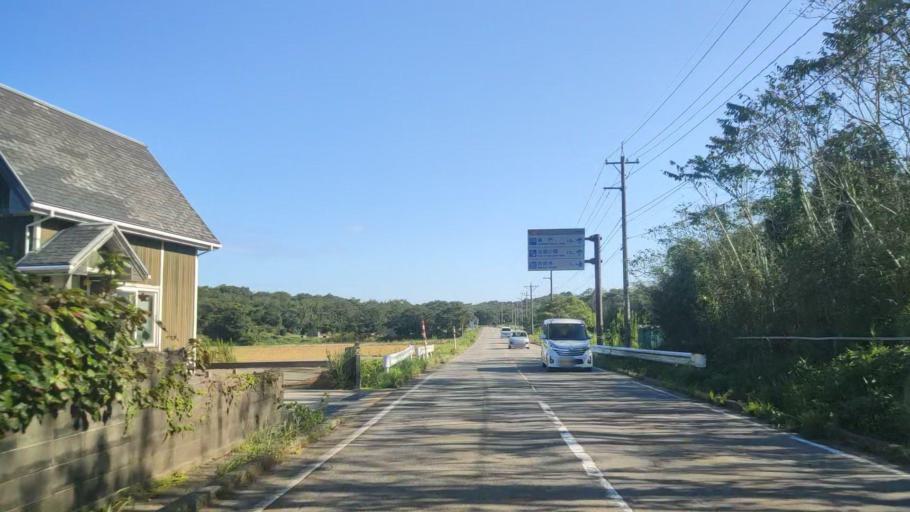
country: JP
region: Ishikawa
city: Hakui
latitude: 36.9582
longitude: 136.7713
